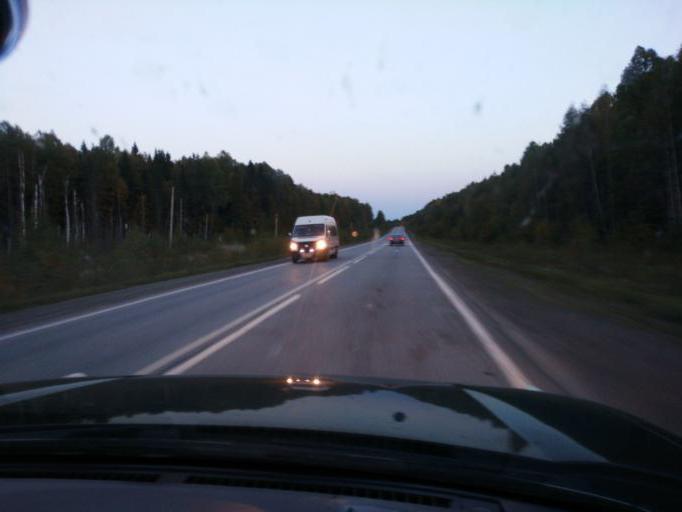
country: RU
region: Perm
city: Verkhnechusovskiye Gorodki
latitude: 58.2686
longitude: 56.9546
